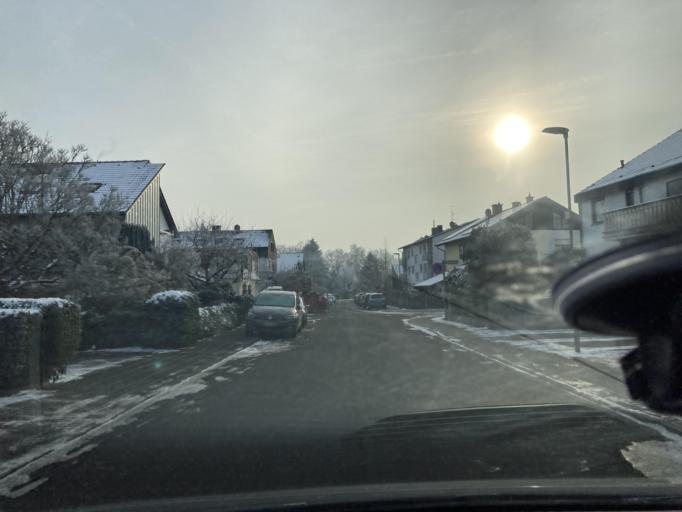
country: DE
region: Hesse
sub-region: Regierungsbezirk Darmstadt
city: Muehlheim am Main
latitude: 50.1262
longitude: 8.8244
